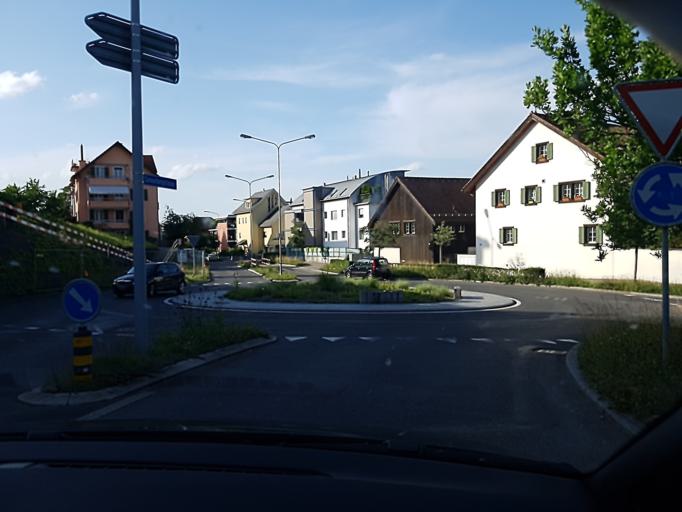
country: CH
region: Zurich
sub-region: Bezirk Horgen
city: Thalwil / Nord
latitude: 47.2977
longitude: 8.5597
